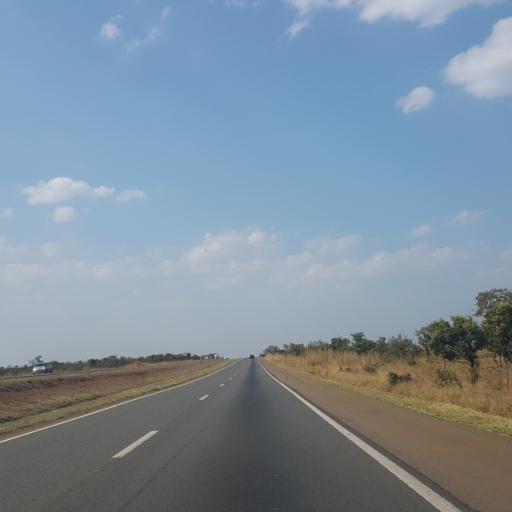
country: BR
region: Goias
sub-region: Abadiania
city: Abadiania
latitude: -16.2019
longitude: -48.7378
